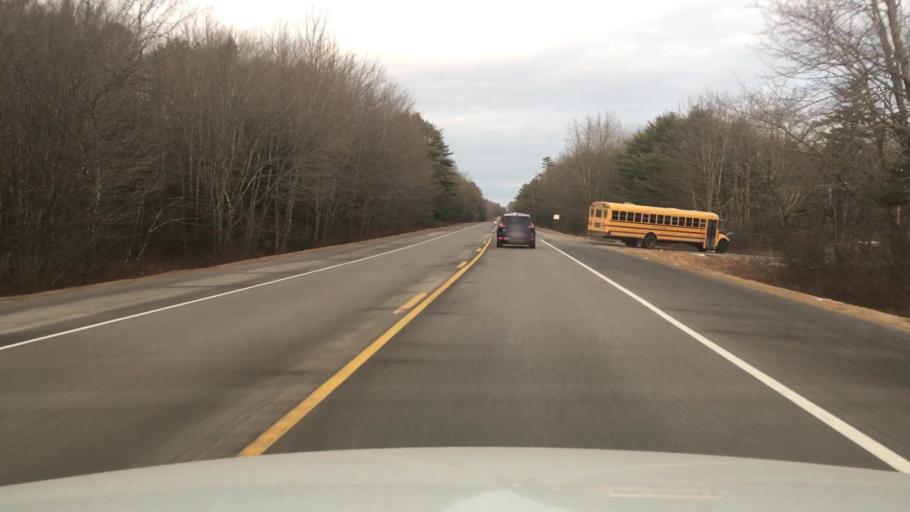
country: US
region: Maine
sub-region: Sagadahoc County
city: Woolwich
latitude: 43.9474
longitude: -69.7501
